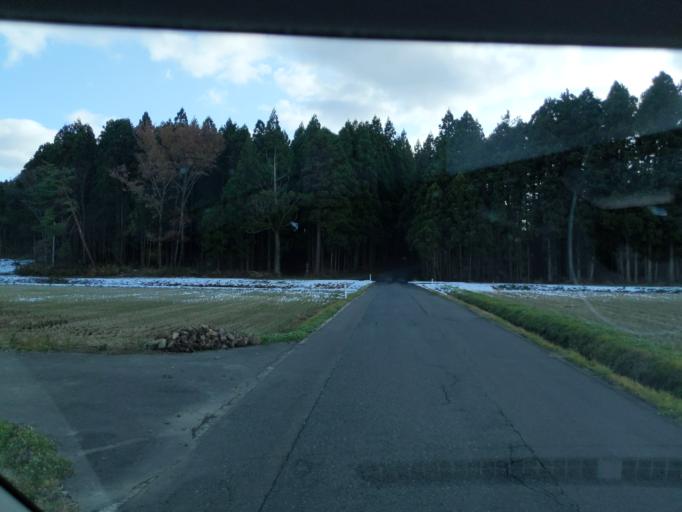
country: JP
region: Iwate
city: Mizusawa
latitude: 39.1164
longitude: 141.0825
